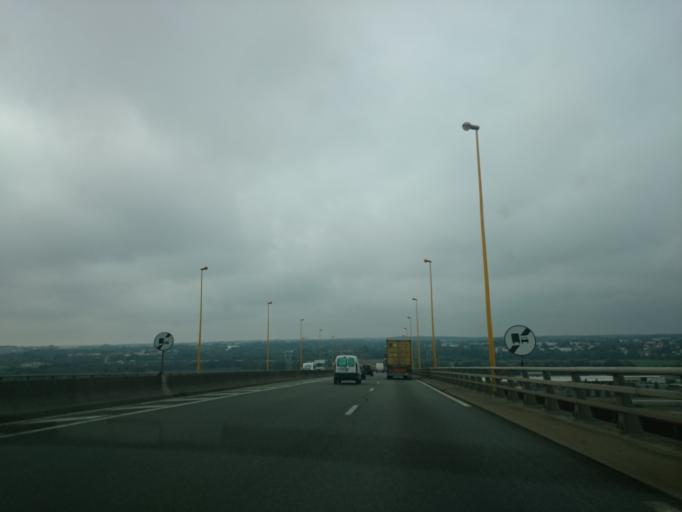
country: FR
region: Pays de la Loire
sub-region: Departement de la Loire-Atlantique
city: Bouguenais
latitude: 47.1909
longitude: -1.6137
